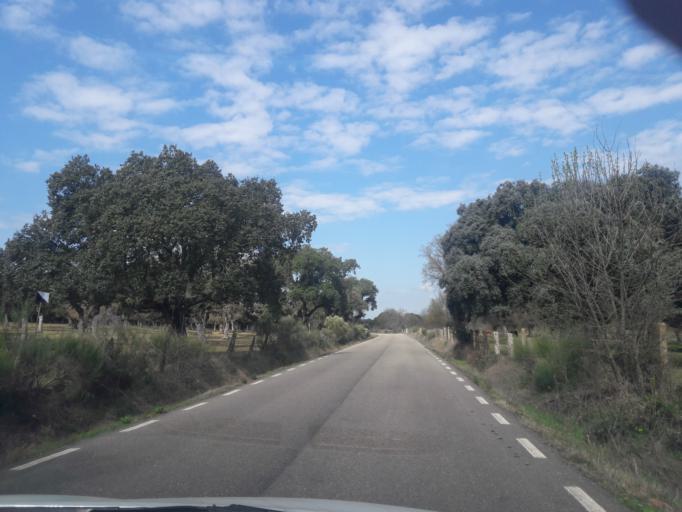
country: ES
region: Castille and Leon
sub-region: Provincia de Salamanca
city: Zamarra
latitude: 40.5533
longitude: -6.4444
